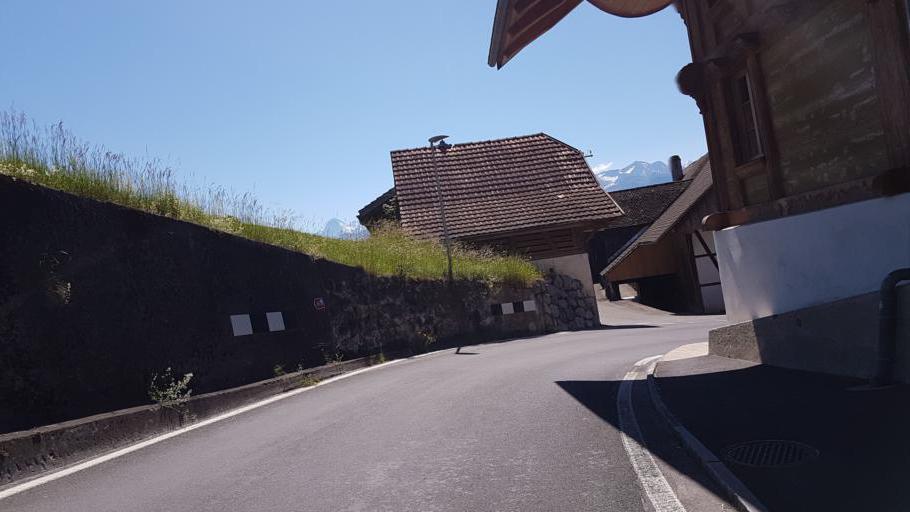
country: CH
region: Bern
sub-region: Frutigen-Niedersimmental District
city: Wimmis
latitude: 46.7047
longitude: 7.6258
